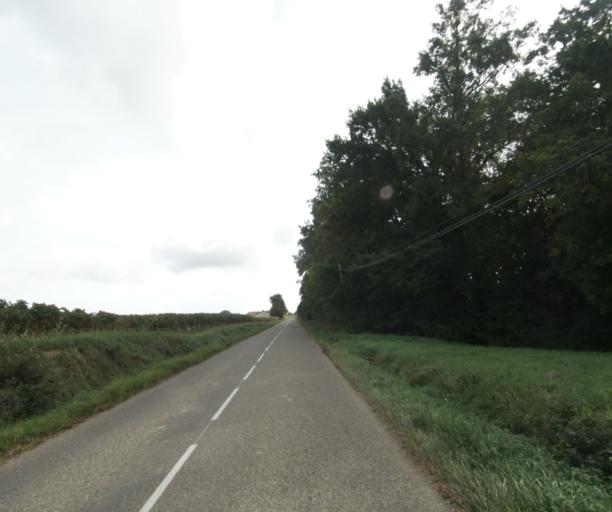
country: FR
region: Midi-Pyrenees
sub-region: Departement du Gers
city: Eauze
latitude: 43.8482
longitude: 0.1336
